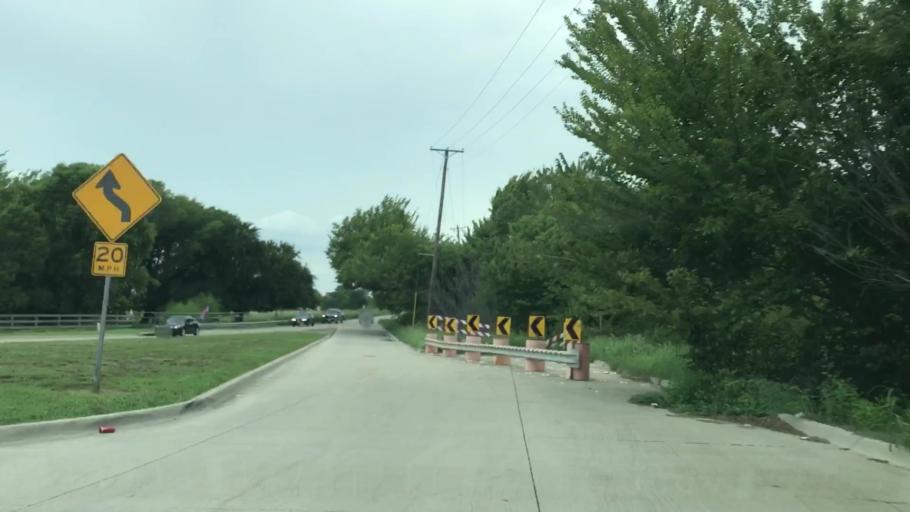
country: US
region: Texas
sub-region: Collin County
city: Frisco
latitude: 33.1897
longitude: -96.7997
